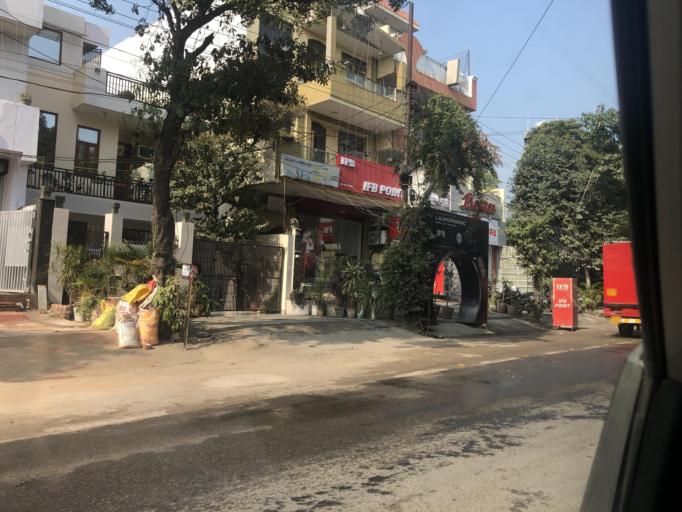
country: IN
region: Uttar Pradesh
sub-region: Gautam Buddha Nagar
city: Noida
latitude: 28.6471
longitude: 77.3597
